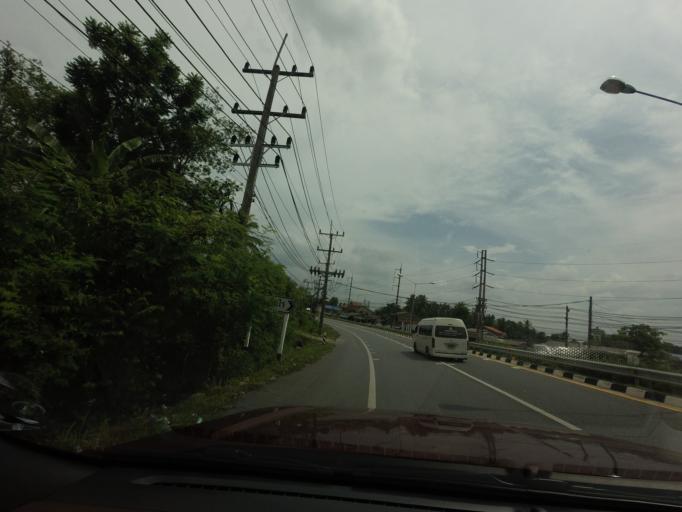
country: TH
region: Yala
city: Yala
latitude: 6.5006
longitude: 101.2683
